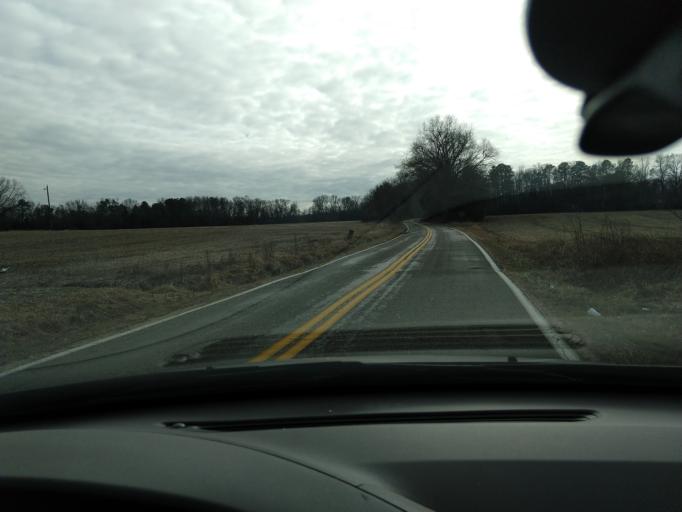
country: US
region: Virginia
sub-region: Henrico County
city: Fort Lee
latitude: 37.4403
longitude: -77.2351
